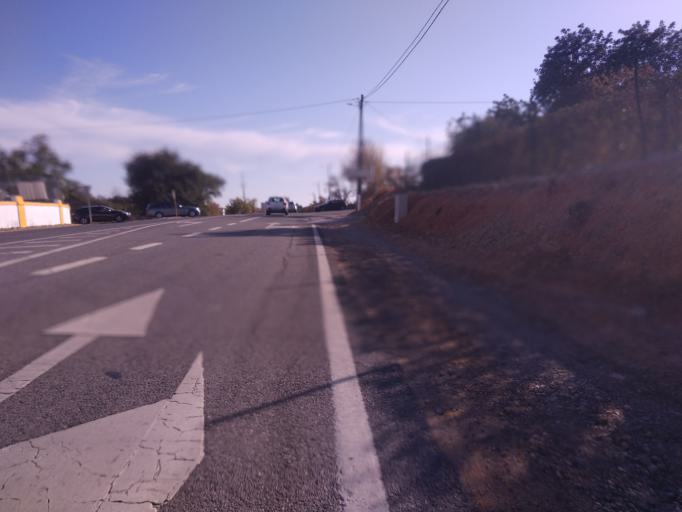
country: PT
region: Faro
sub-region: Faro
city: Santa Barbara de Nexe
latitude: 37.0954
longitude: -7.9069
